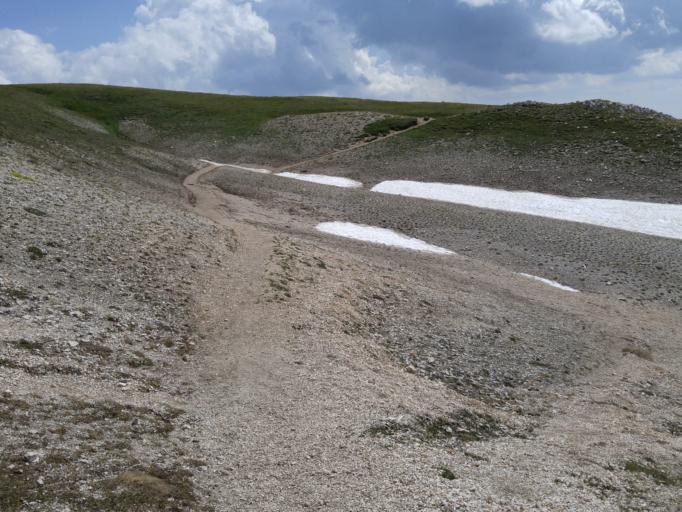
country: IT
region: Abruzzo
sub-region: Provincia di Teramo
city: Pietracamela
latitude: 42.4593
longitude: 13.5641
